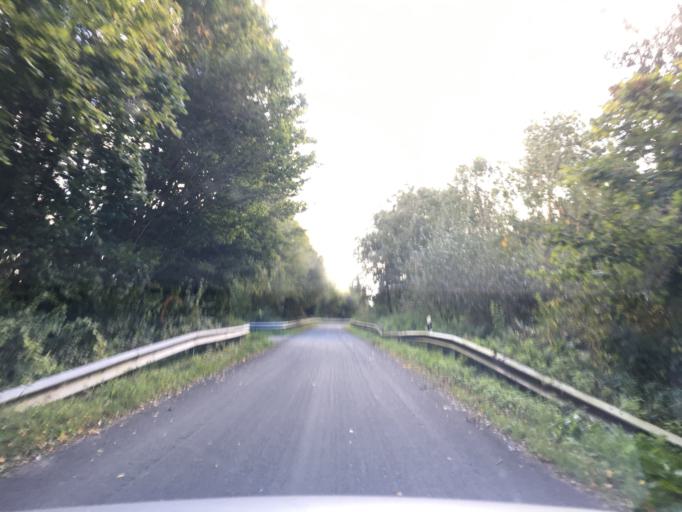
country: DE
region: Schleswig-Holstein
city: Melsdorf
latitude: 54.3131
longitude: 10.0087
